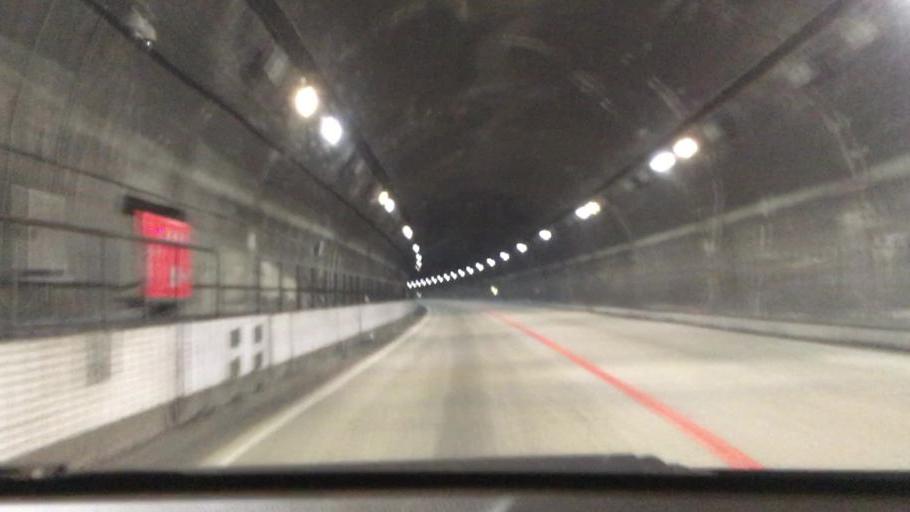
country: JP
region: Yamaguchi
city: Tokuyama
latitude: 34.0686
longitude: 131.8281
